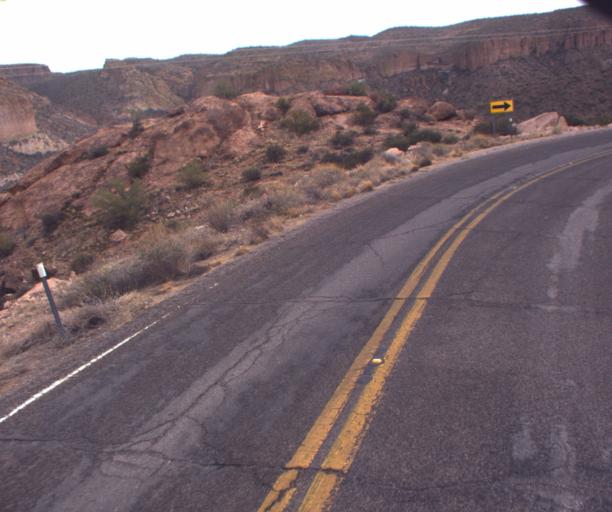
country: US
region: Arizona
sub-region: Pinal County
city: Apache Junction
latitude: 33.5286
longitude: -111.4007
